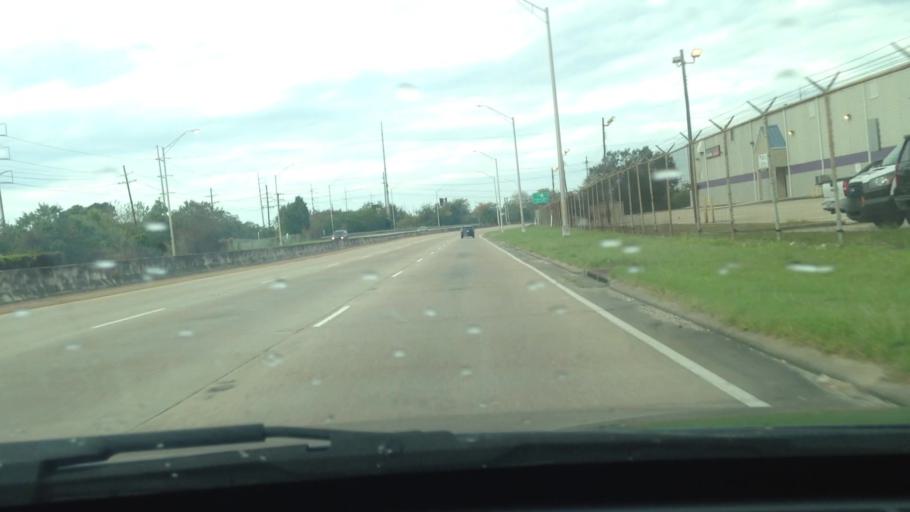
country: US
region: Louisiana
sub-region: Jefferson Parish
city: Jefferson
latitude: 29.9703
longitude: -90.1494
